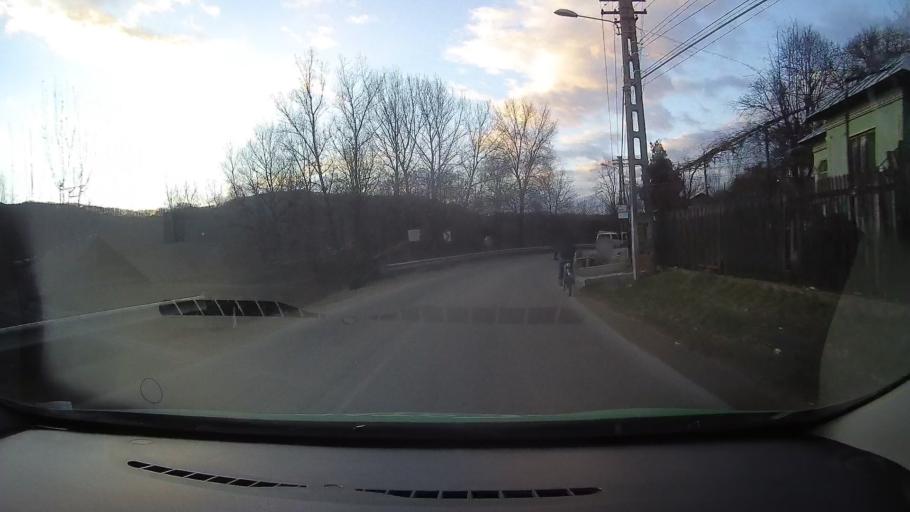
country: RO
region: Dambovita
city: Iedera de Jos
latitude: 45.0183
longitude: 25.6391
